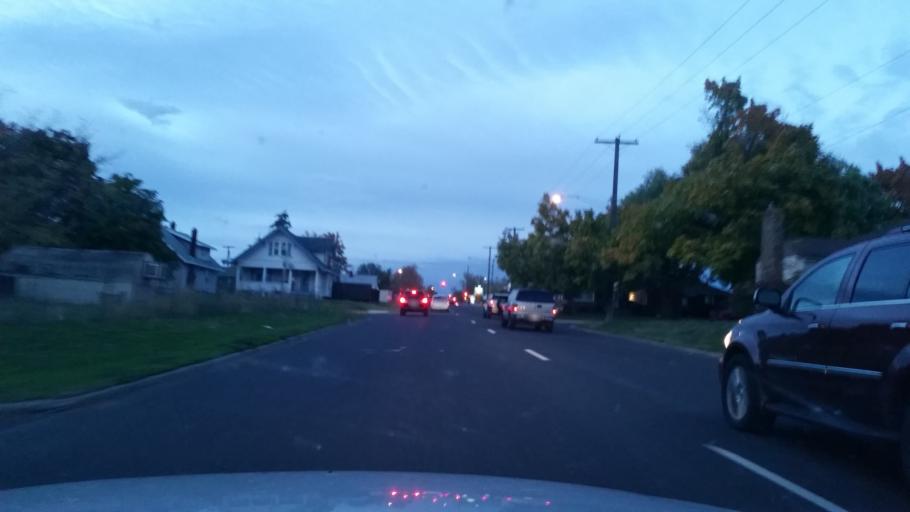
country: US
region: Washington
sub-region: Spokane County
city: Spokane
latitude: 47.6916
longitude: -117.4351
